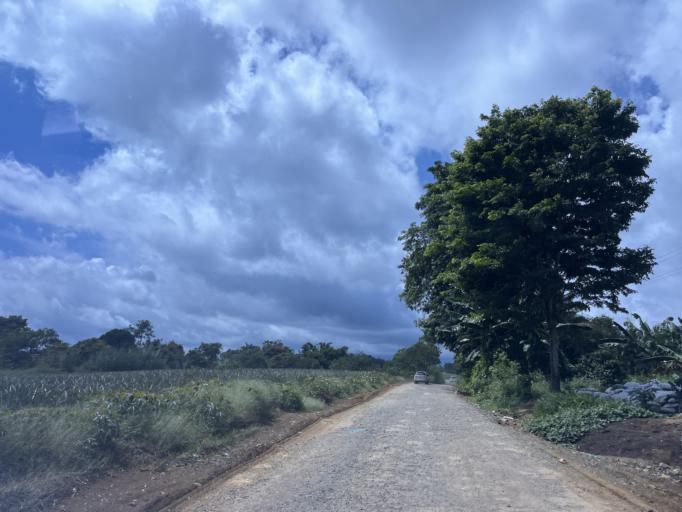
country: PH
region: Northern Mindanao
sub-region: Province of Bukidnon
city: Impalutao
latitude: 8.2472
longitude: 125.0005
